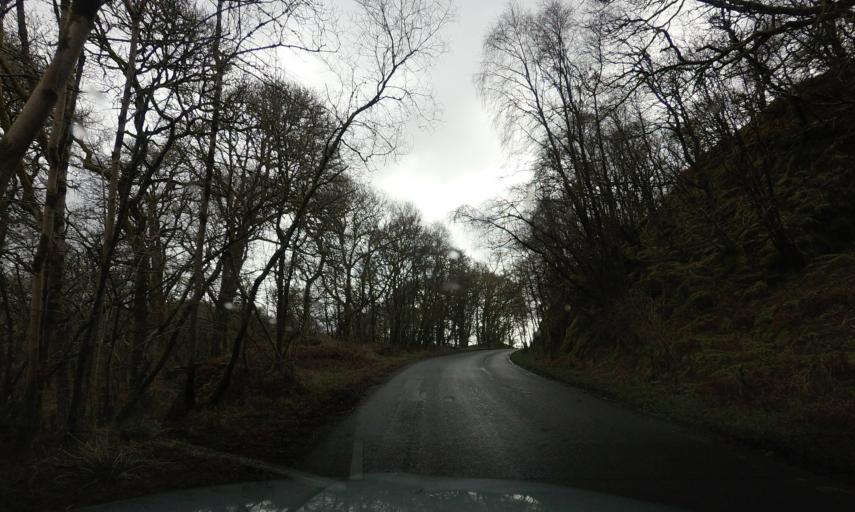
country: GB
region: Scotland
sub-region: West Dunbartonshire
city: Balloch
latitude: 56.0942
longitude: -4.5527
